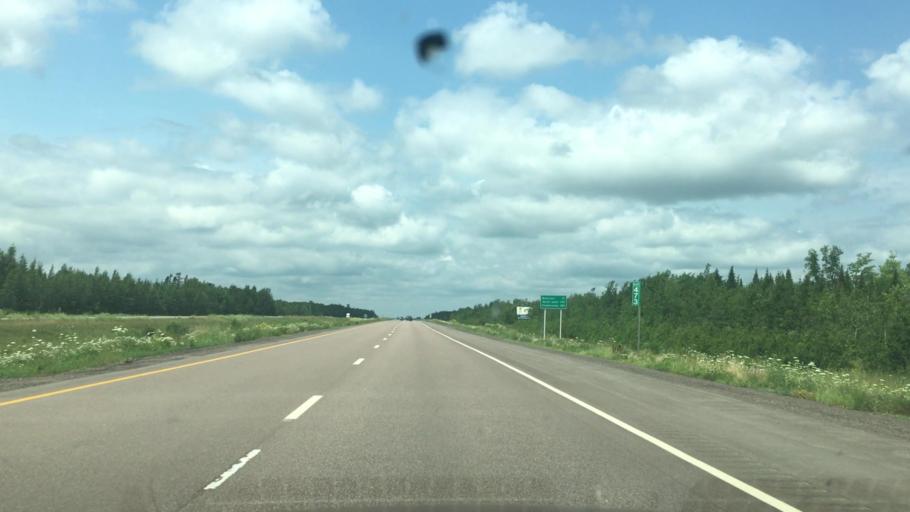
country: CA
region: New Brunswick
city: Dieppe
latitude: 46.1097
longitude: -64.6114
